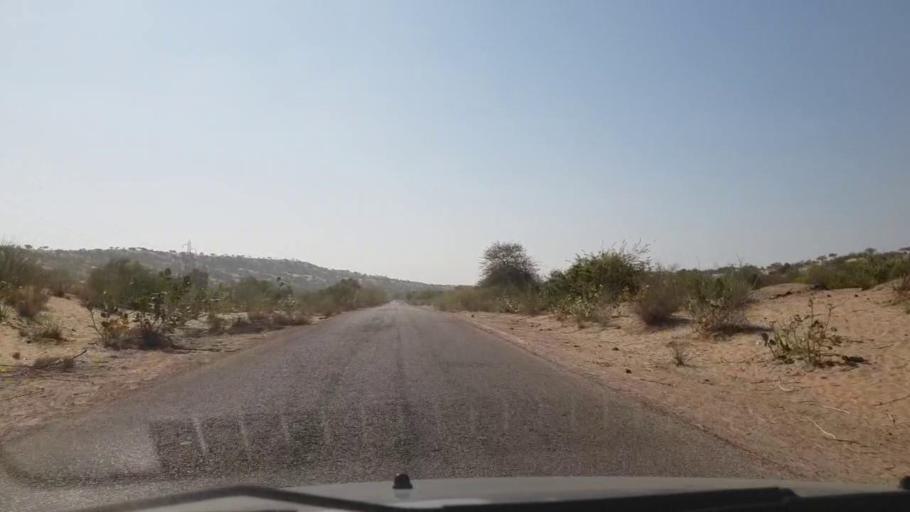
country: PK
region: Sindh
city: Diplo
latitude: 24.5855
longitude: 69.7057
